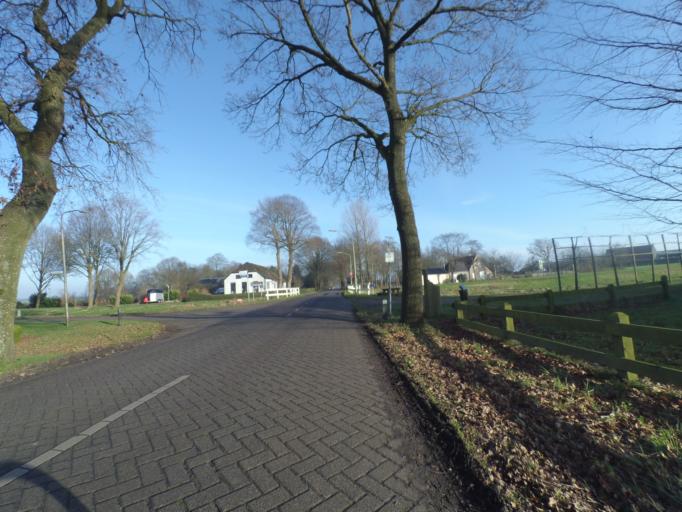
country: NL
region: Drenthe
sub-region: Gemeente Borger-Odoorn
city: Borger
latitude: 52.8671
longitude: 6.7635
